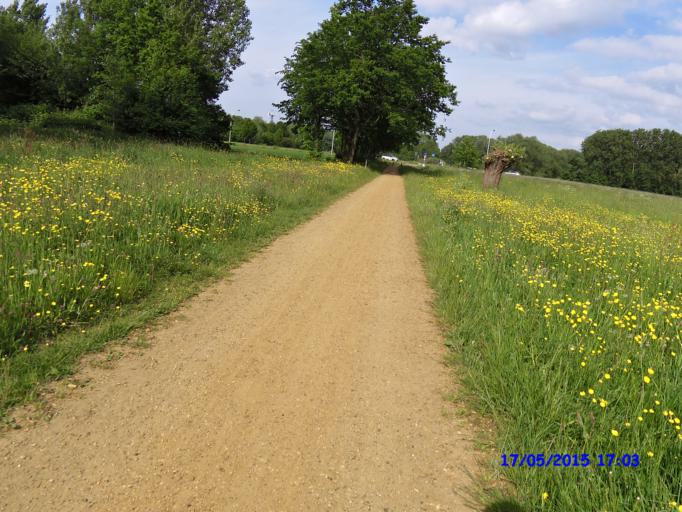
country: BE
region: Flanders
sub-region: Provincie Antwerpen
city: Aartselaar
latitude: 51.1557
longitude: 4.3998
